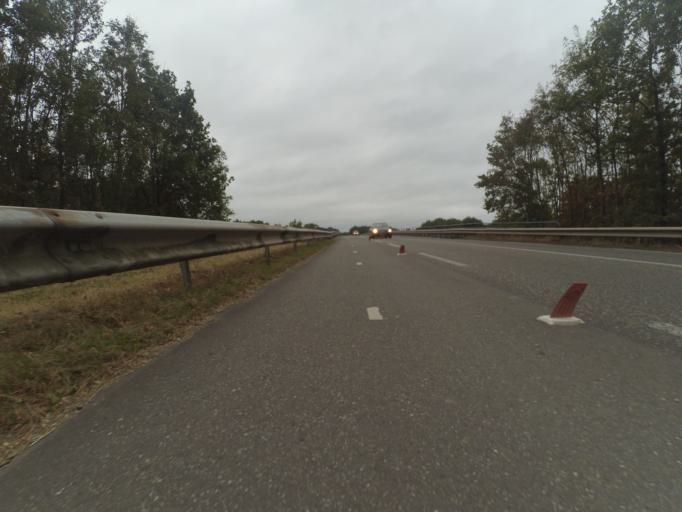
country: NL
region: Gelderland
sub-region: Gemeente Tiel
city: Tiel
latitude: 51.9246
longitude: 5.4278
